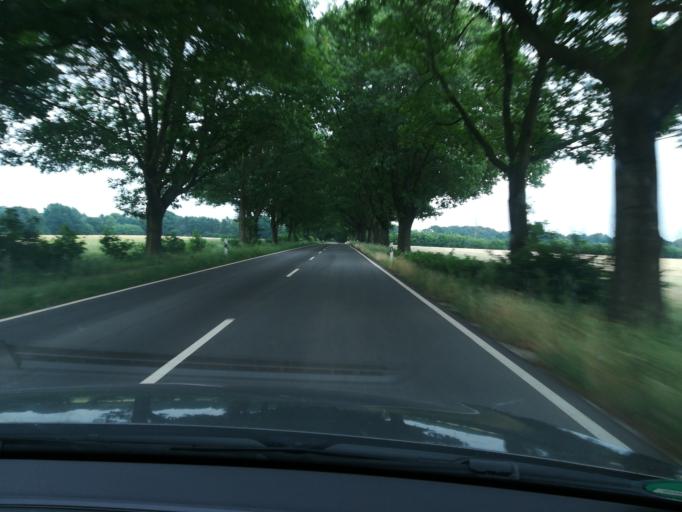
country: DE
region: Schleswig-Holstein
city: Grossensee
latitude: 53.6246
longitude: 10.3283
